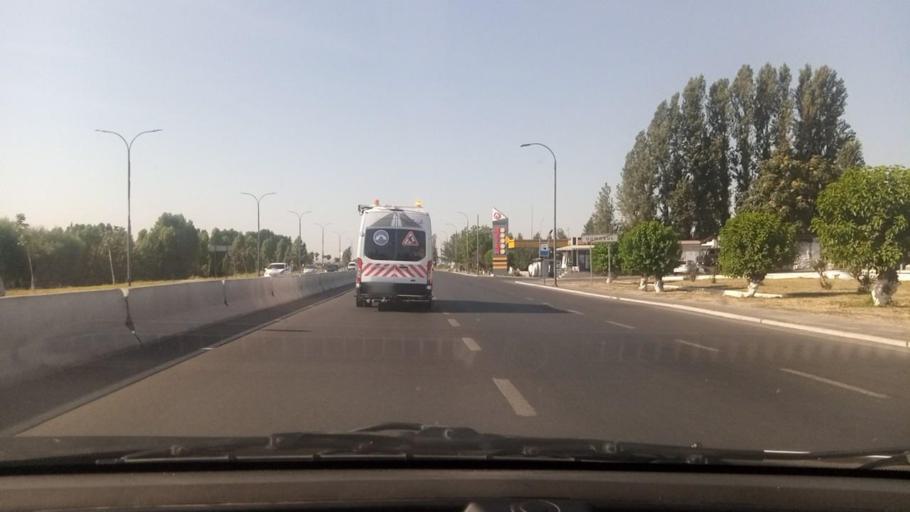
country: UZ
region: Toshkent Shahri
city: Bektemir
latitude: 41.2061
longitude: 69.3327
